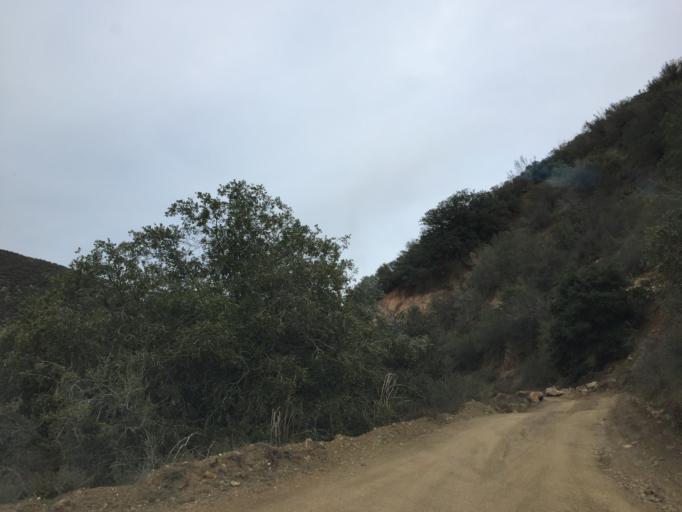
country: US
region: California
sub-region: San Bernardino County
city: Yucaipa
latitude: 34.1125
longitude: -117.0337
